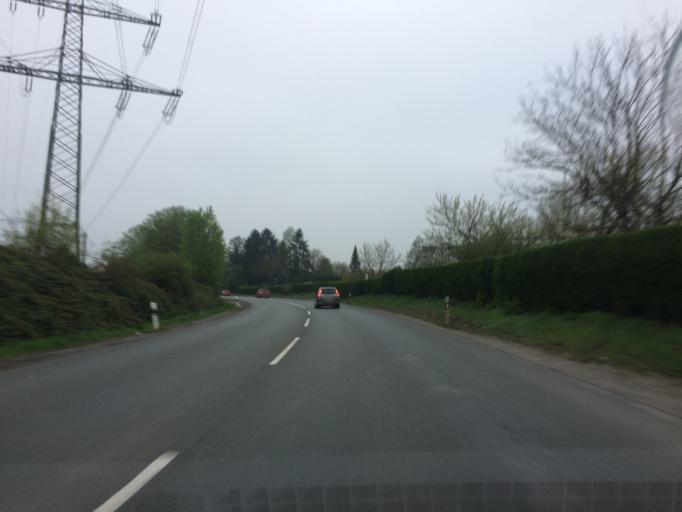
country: DE
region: North Rhine-Westphalia
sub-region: Regierungsbezirk Munster
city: Gelsenkirchen
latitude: 51.4949
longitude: 7.0980
